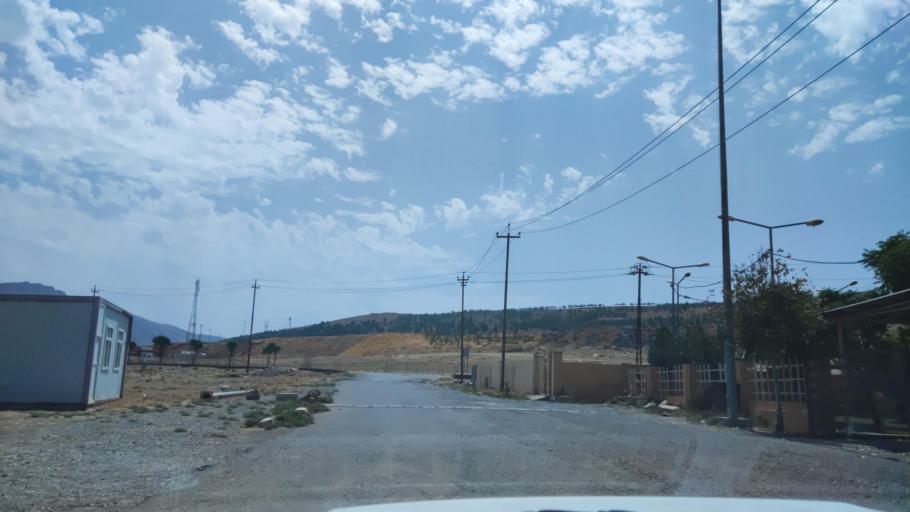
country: IQ
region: Arbil
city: Shaqlawah
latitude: 36.4972
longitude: 44.3612
